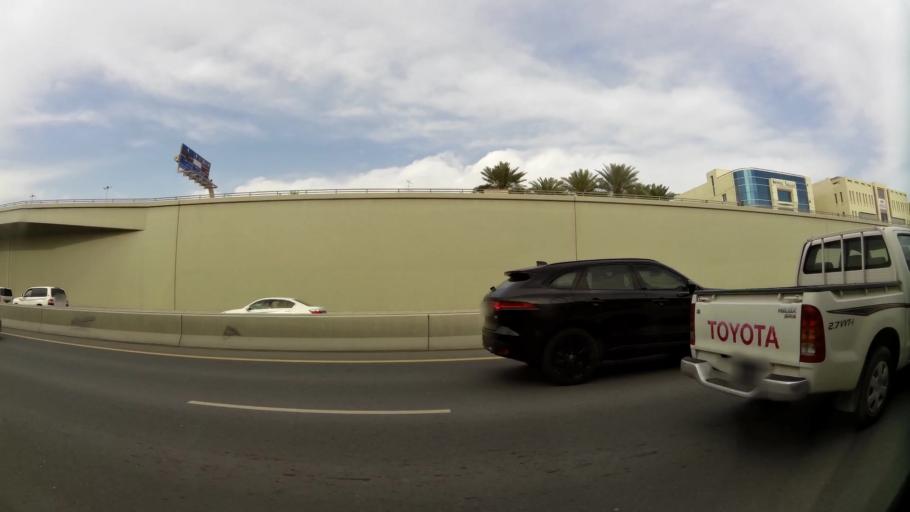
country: QA
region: Baladiyat ad Dawhah
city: Doha
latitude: 25.2746
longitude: 51.4899
